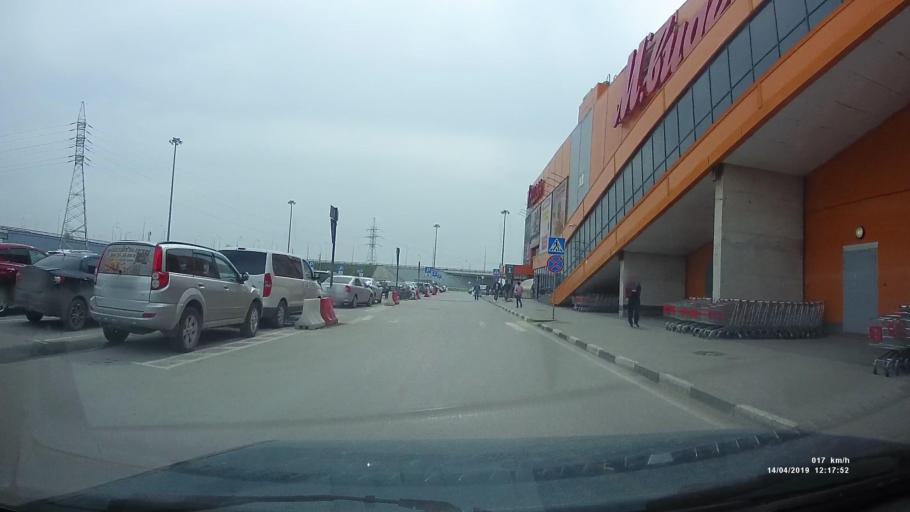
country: RU
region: Rostov
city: Rostov-na-Donu
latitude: 47.2050
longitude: 39.7257
